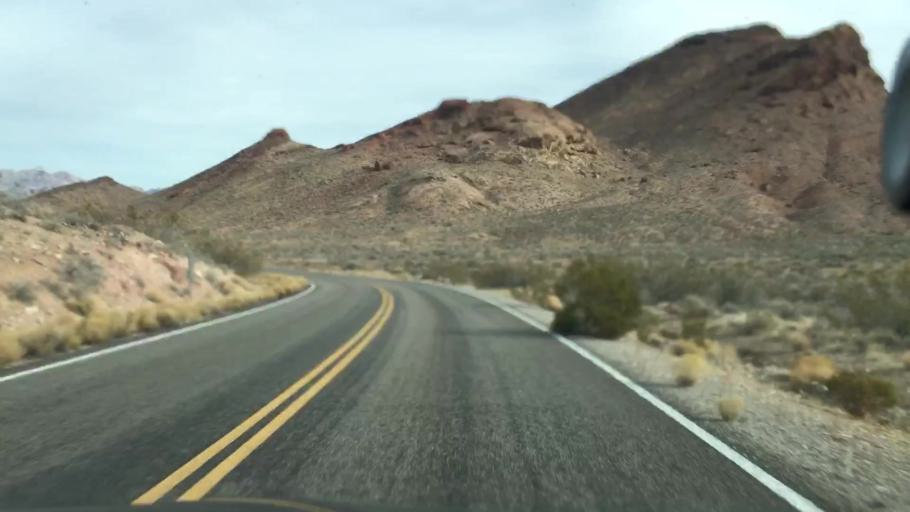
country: US
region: Nevada
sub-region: Nye County
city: Beatty
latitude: 36.7938
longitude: -116.9219
